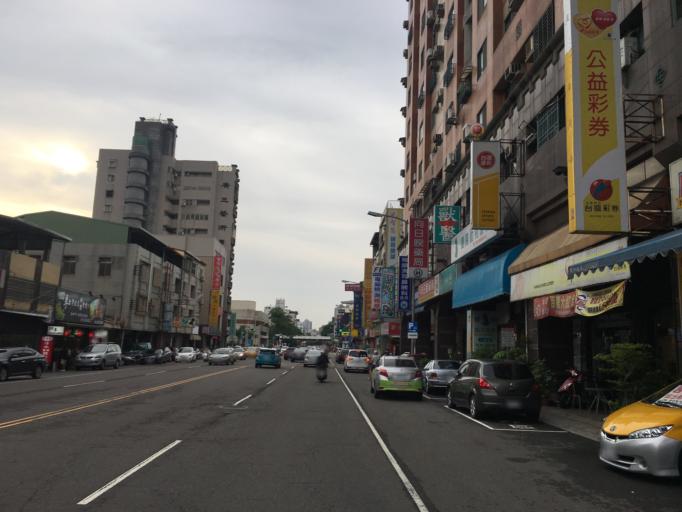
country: TW
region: Taiwan
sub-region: Taichung City
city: Taichung
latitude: 24.1376
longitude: 120.6709
